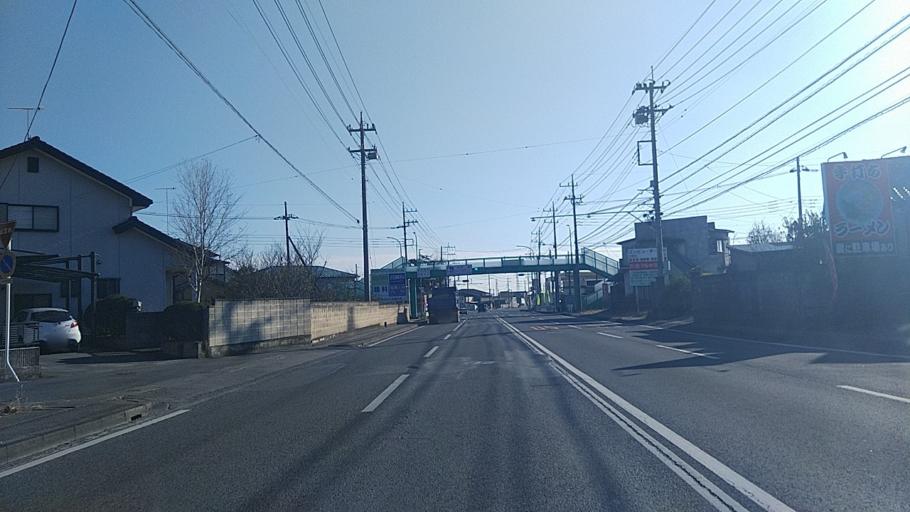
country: JP
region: Tochigi
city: Tanuma
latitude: 36.3635
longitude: 139.5753
